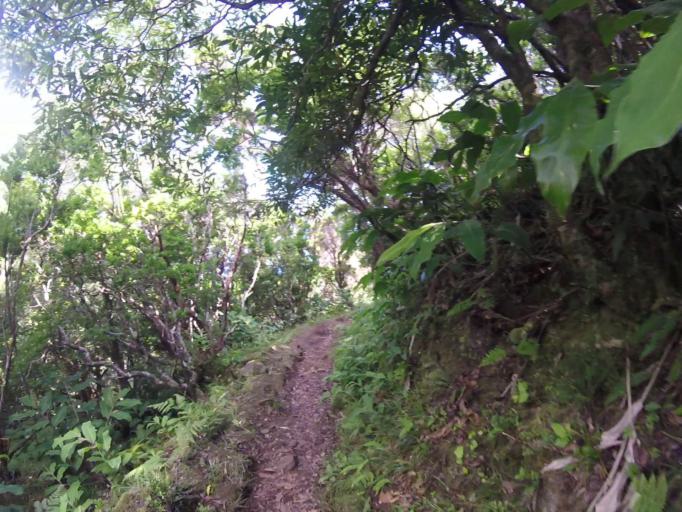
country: PT
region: Azores
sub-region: Sao Roque do Pico
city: Sao Roque do Pico
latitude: 38.6065
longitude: -27.9207
